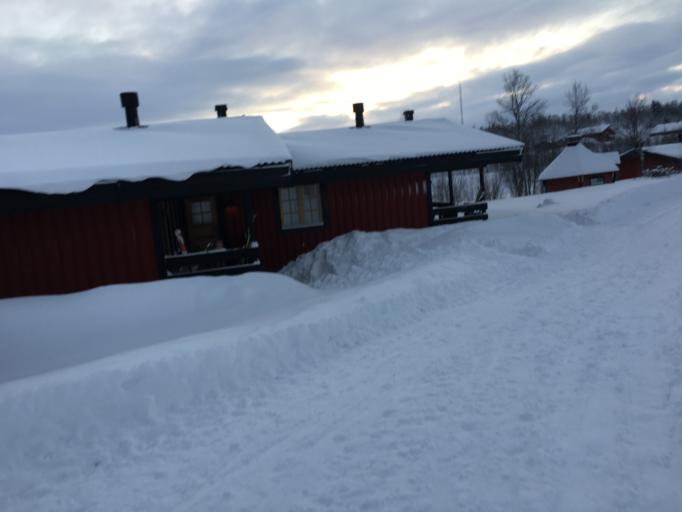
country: NO
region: Nord-Trondelag
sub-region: Meraker
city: Meraker
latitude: 63.3197
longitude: 12.0891
